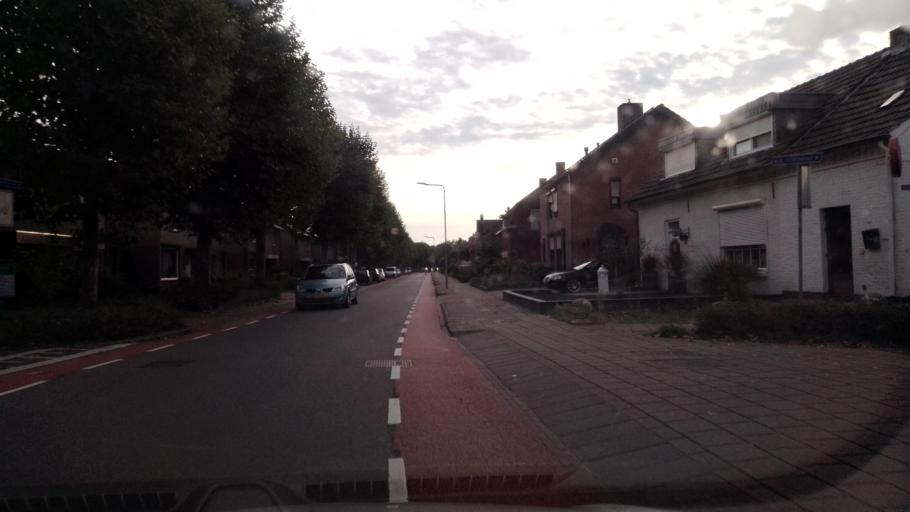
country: NL
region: Limburg
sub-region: Gemeente Venlo
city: Tegelen
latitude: 51.3145
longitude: 6.1250
